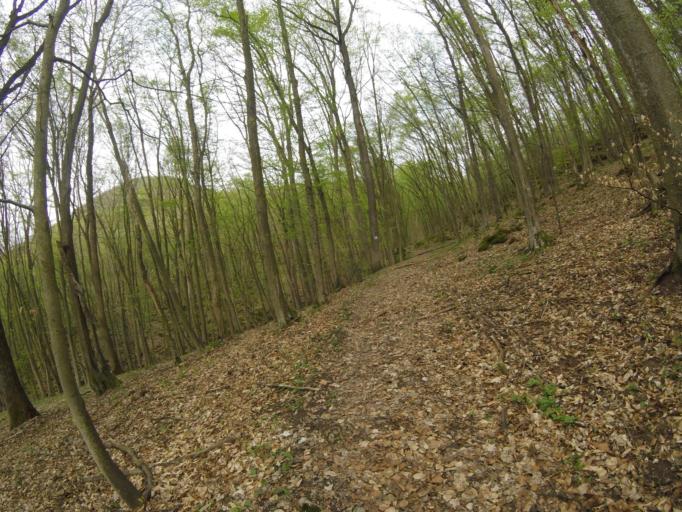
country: HU
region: Borsod-Abauj-Zemplen
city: Szendro
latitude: 48.5439
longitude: 20.6718
